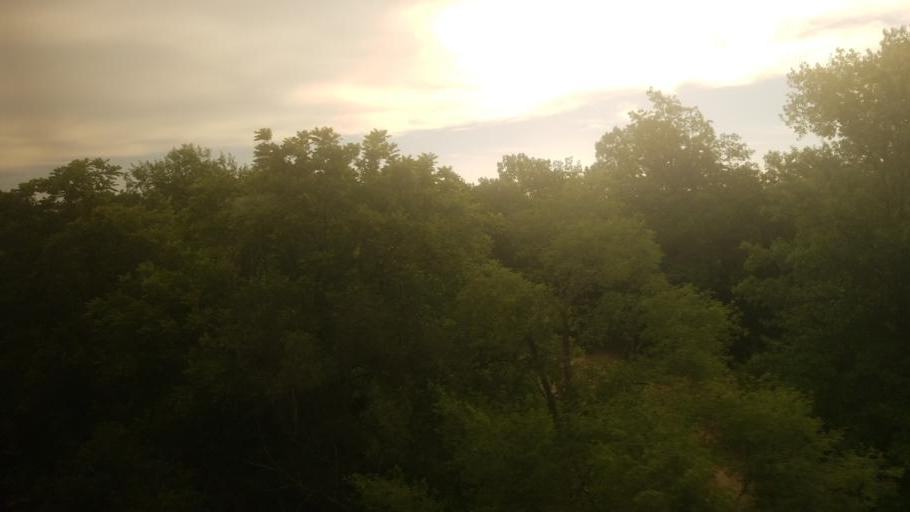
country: US
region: Kansas
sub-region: Shawnee County
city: Topeka
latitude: 39.0060
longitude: -95.6815
